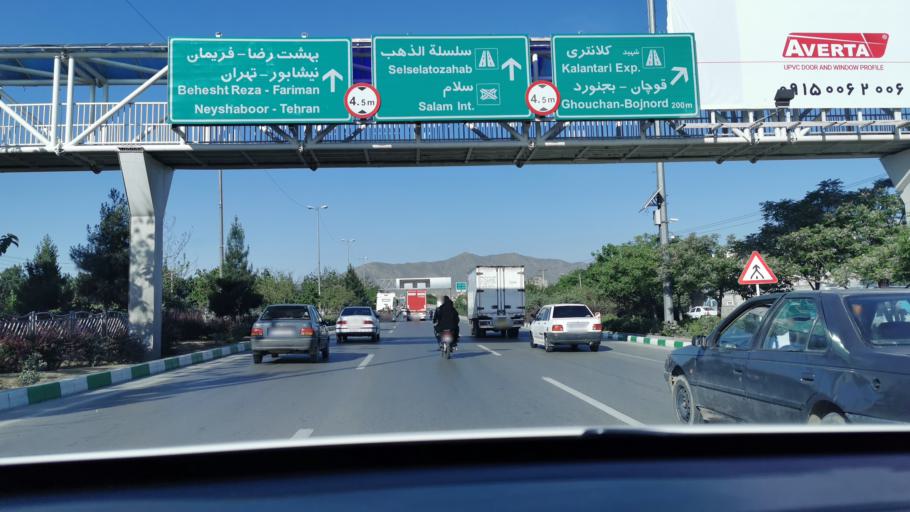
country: IR
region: Razavi Khorasan
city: Mashhad
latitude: 36.2560
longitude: 59.6201
